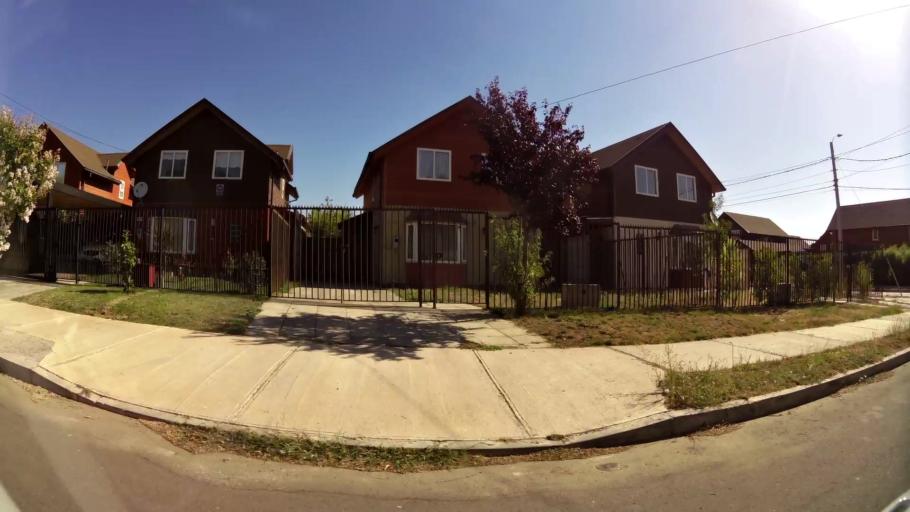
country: CL
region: Maule
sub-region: Provincia de Talca
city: Talca
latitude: -35.4178
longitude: -71.6144
